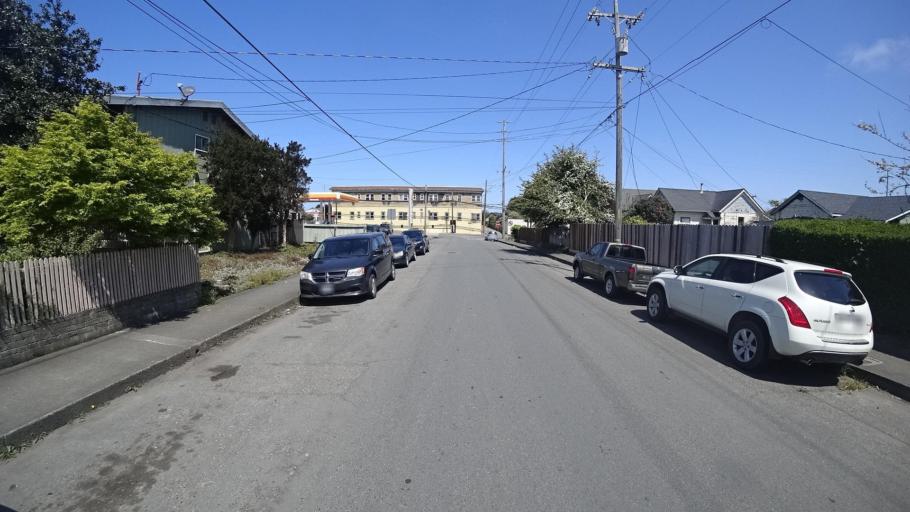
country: US
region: California
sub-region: Humboldt County
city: Bayview
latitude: 40.7799
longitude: -124.1716
